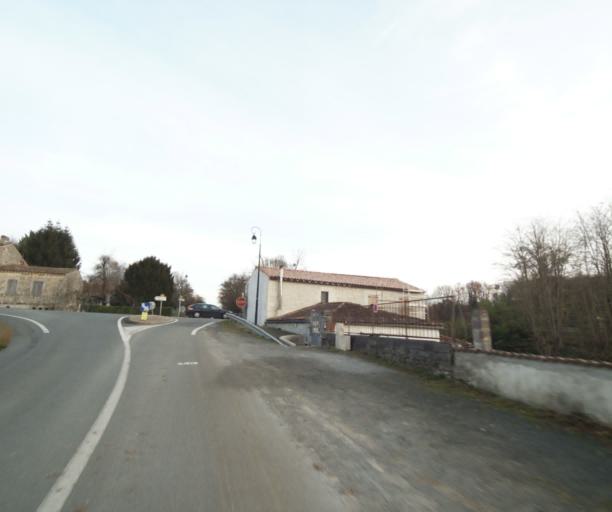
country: FR
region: Poitou-Charentes
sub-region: Departement de la Charente-Maritime
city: Fontcouverte
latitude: 45.7955
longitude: -0.5674
